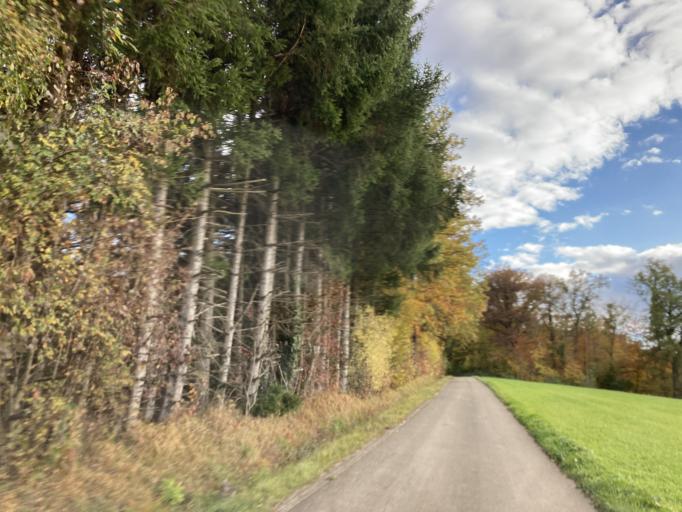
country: DE
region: Baden-Wuerttemberg
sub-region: Tuebingen Region
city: Dusslingen
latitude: 48.4783
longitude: 9.0696
